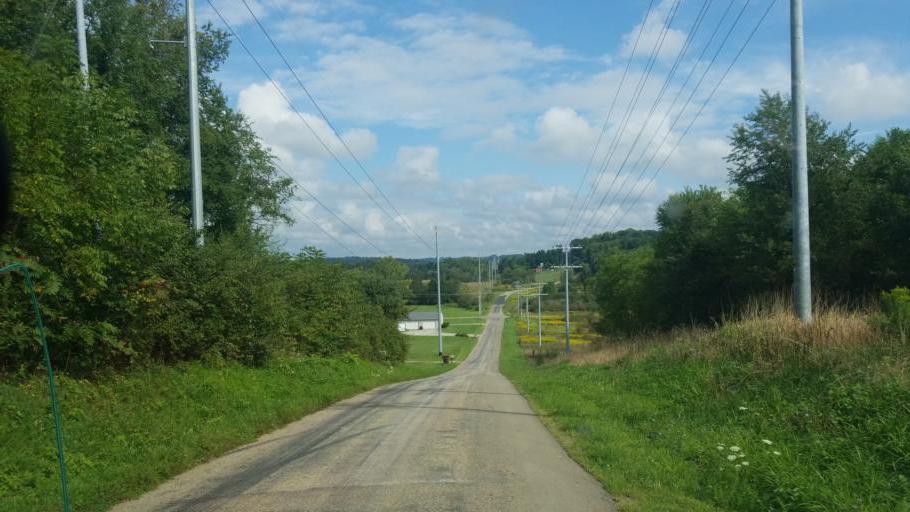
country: US
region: Ohio
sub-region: Knox County
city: Fredericktown
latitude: 40.4714
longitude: -82.4615
